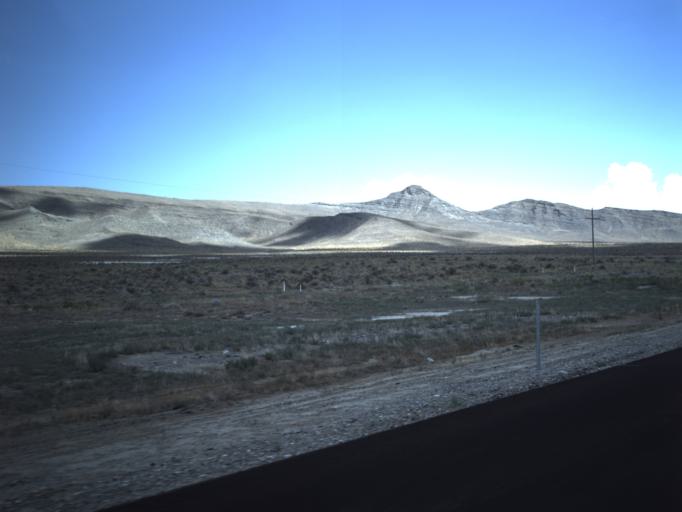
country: US
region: Utah
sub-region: Beaver County
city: Milford
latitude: 39.0487
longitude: -113.4159
